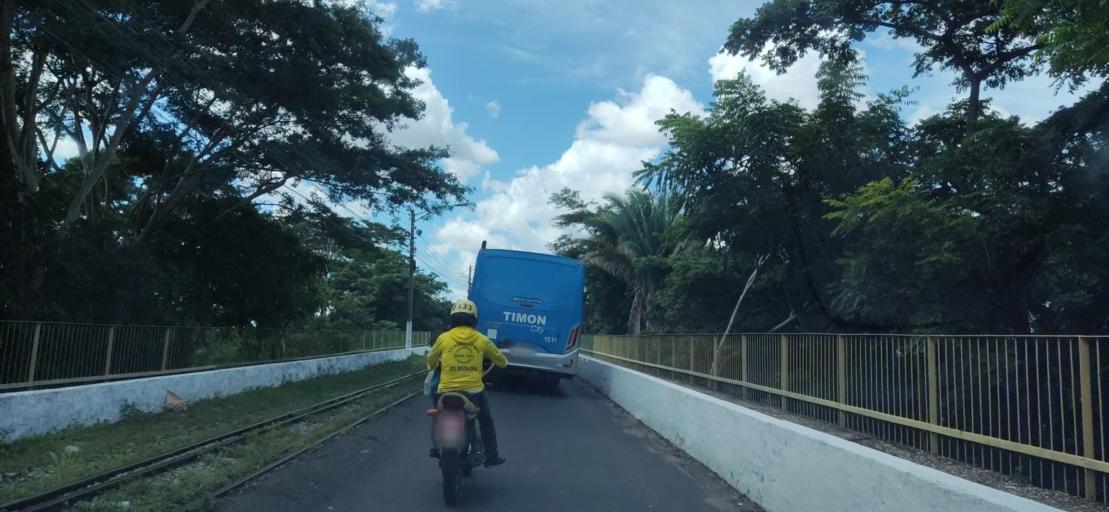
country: BR
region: Maranhao
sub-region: Timon
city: Timon
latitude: -5.0884
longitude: -42.8261
